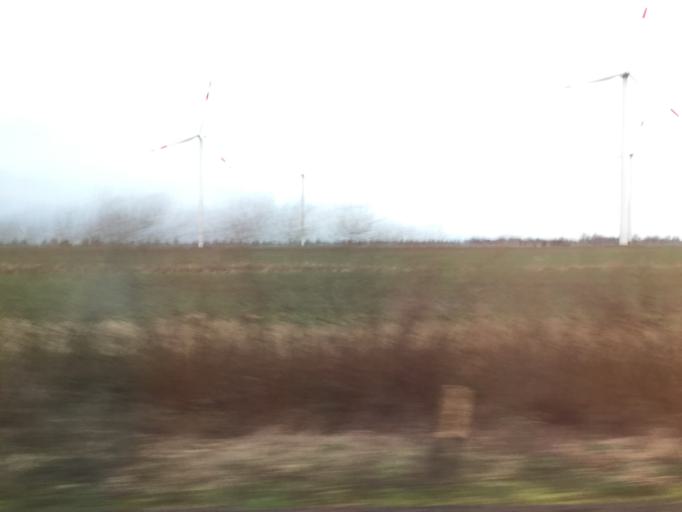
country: DE
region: Schleswig-Holstein
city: Sommerland
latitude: 53.7886
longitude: 9.5233
